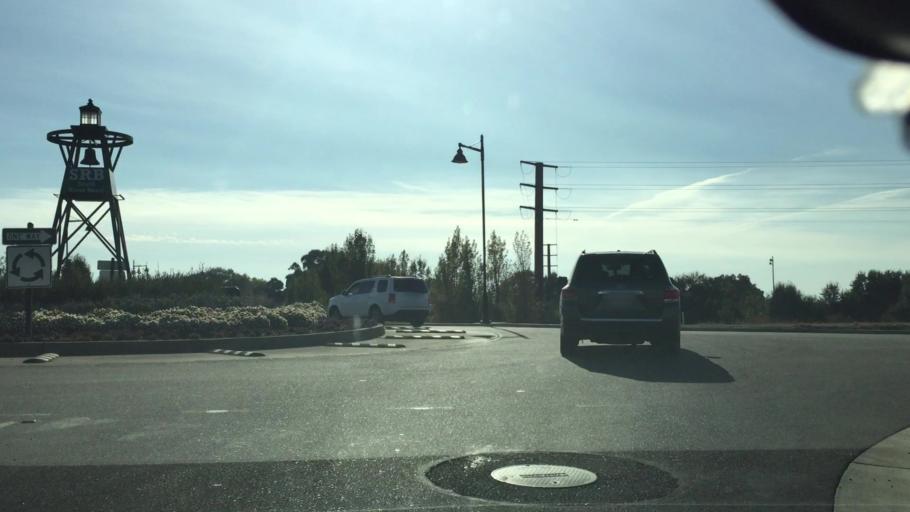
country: US
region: California
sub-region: San Joaquin County
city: Lathrop
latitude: 37.7885
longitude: -121.3107
